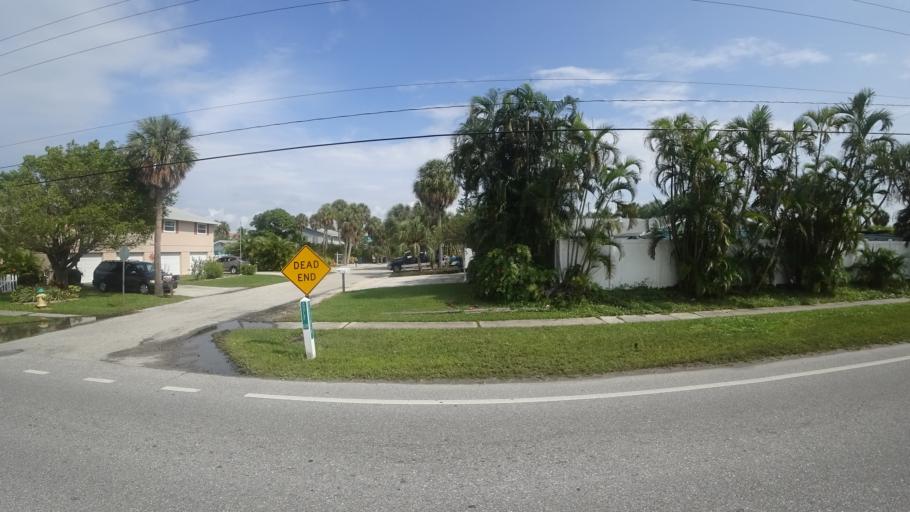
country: US
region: Florida
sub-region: Manatee County
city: Holmes Beach
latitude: 27.5049
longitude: -82.7127
